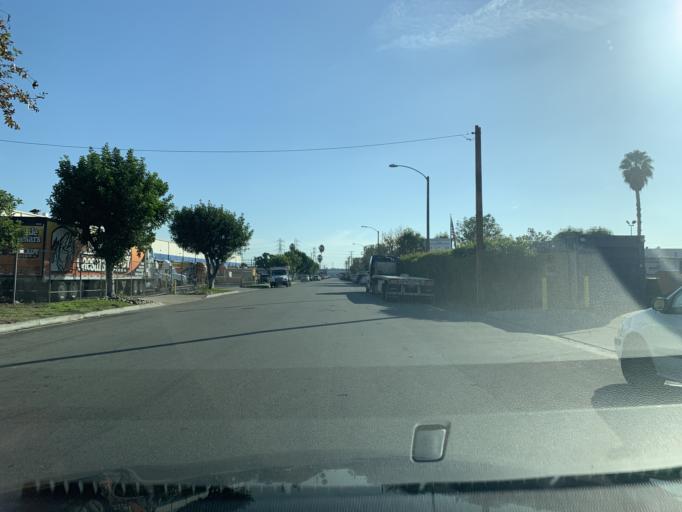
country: US
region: California
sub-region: Orange County
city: Anaheim
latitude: 33.8147
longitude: -117.9002
